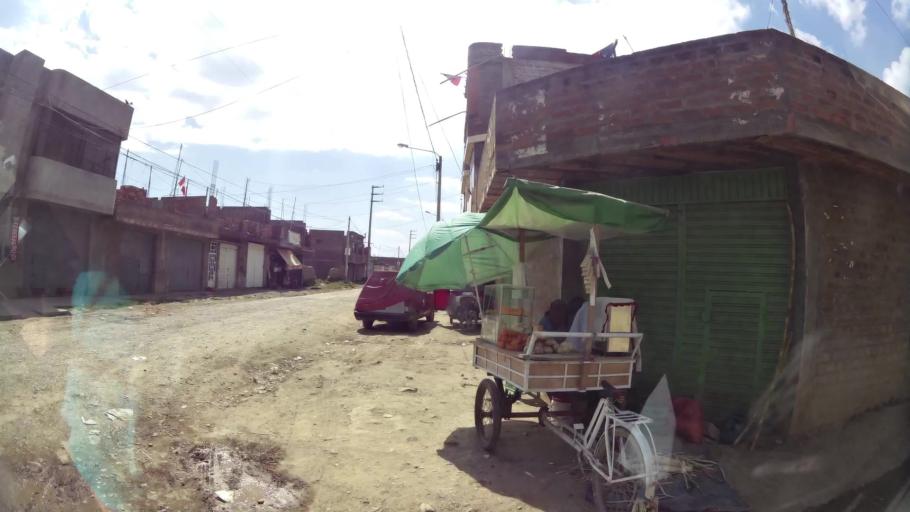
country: PE
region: Junin
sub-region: Provincia de Huancayo
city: Huancayo
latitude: -12.0952
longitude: -75.2001
